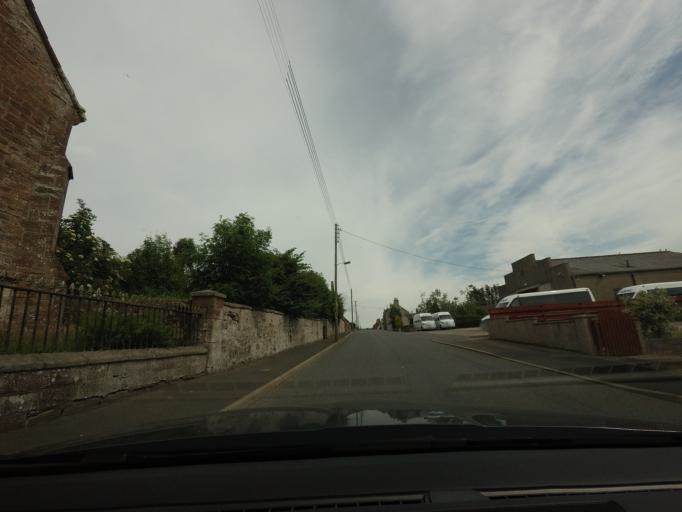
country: GB
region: Scotland
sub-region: Aberdeenshire
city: Turriff
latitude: 57.5742
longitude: -2.2997
